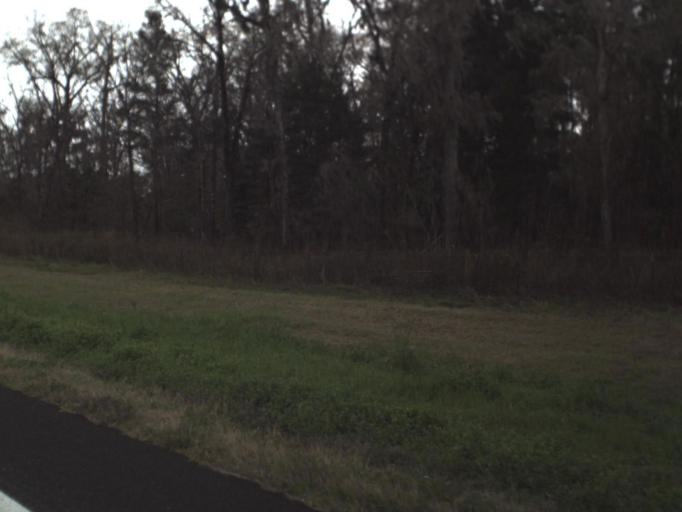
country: US
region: Florida
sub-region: Jefferson County
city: Monticello
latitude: 30.4031
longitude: -83.8862
